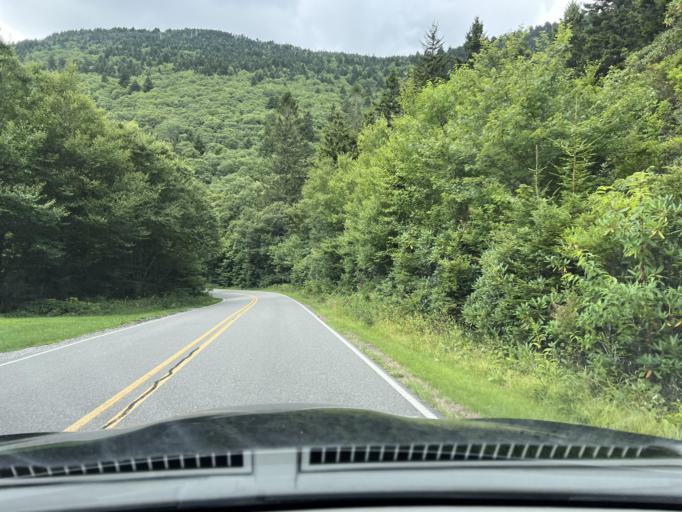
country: US
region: North Carolina
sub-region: Buncombe County
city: Black Mountain
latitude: 35.7298
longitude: -82.2830
